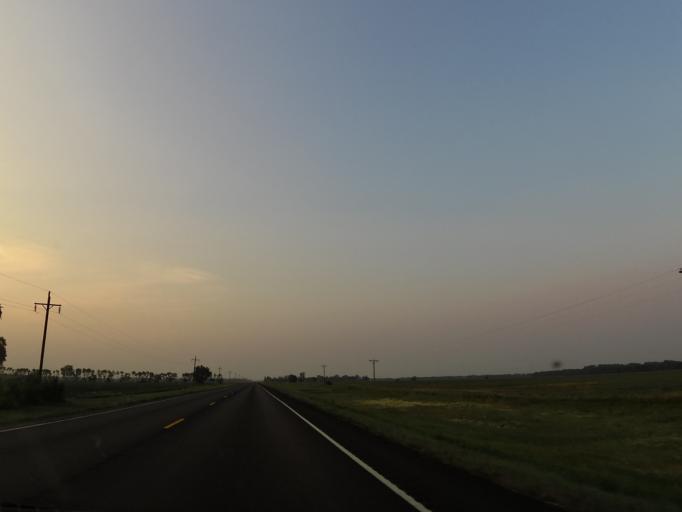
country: US
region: North Dakota
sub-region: Walsh County
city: Park River
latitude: 48.2689
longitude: -97.6225
